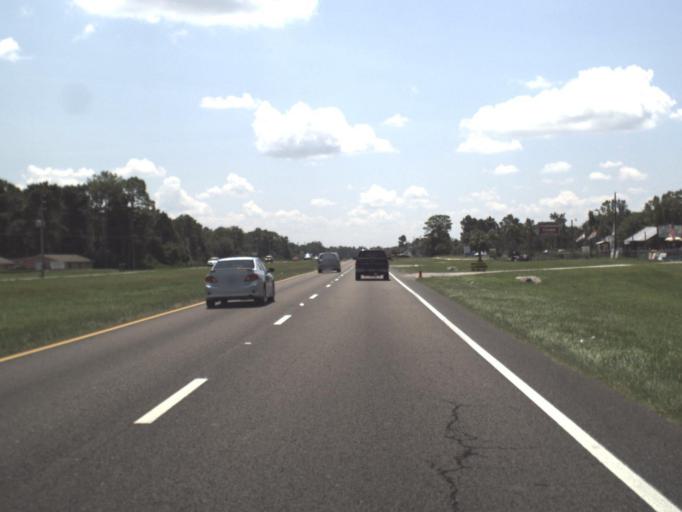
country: US
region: Florida
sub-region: Citrus County
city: Homosassa Springs
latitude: 28.7872
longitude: -82.5644
